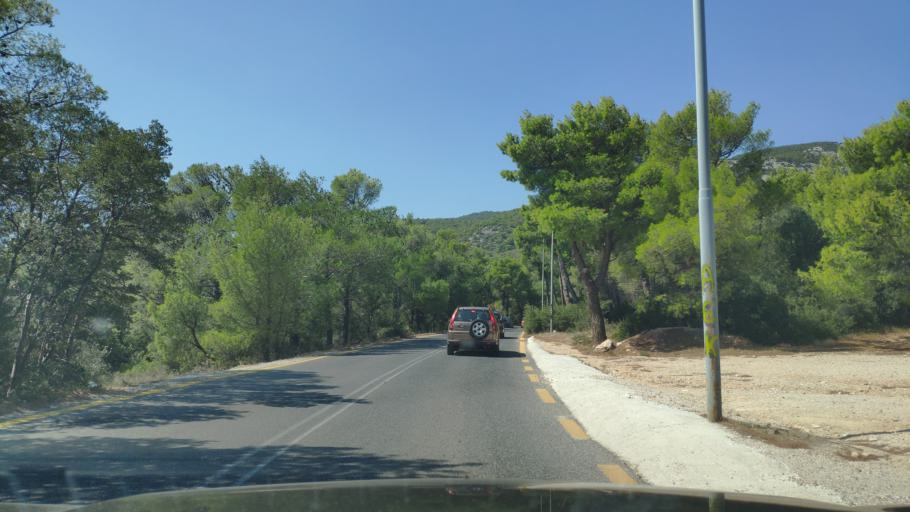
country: GR
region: Attica
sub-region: Nomarchia Anatolikis Attikis
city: Thrakomakedones
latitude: 38.1295
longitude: 23.7359
